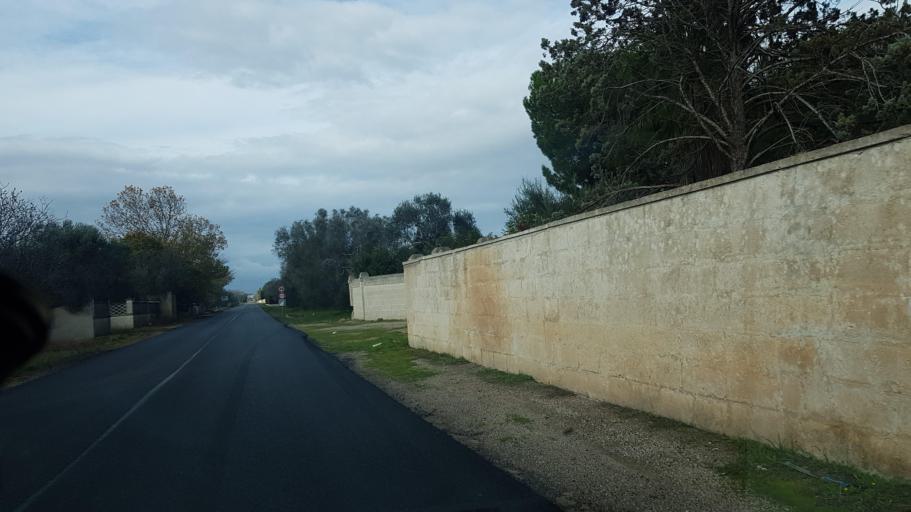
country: IT
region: Apulia
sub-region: Provincia di Brindisi
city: Torre Santa Susanna
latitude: 40.4743
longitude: 17.7058
